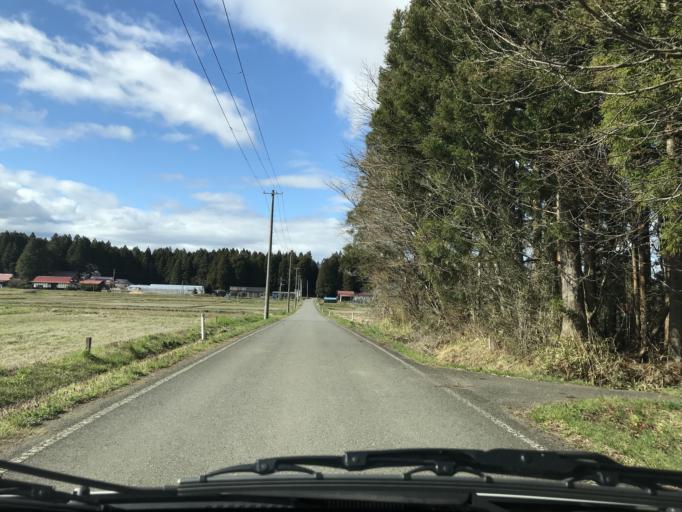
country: JP
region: Iwate
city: Mizusawa
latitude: 39.1072
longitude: 141.0926
